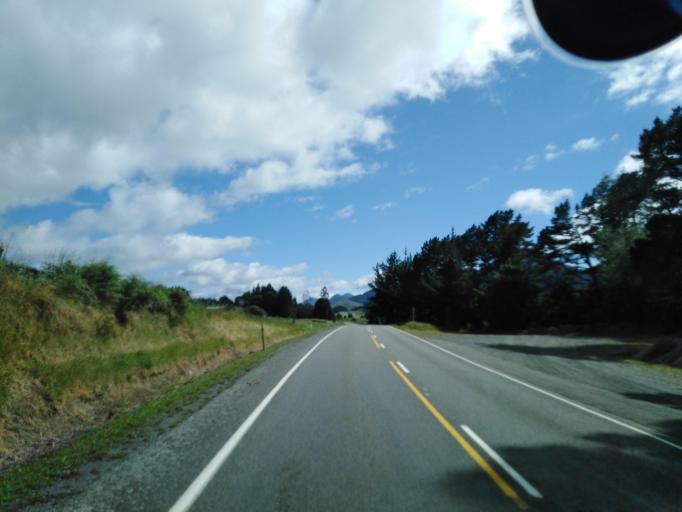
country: NZ
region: Nelson
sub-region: Nelson City
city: Nelson
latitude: -41.2844
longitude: 173.5721
